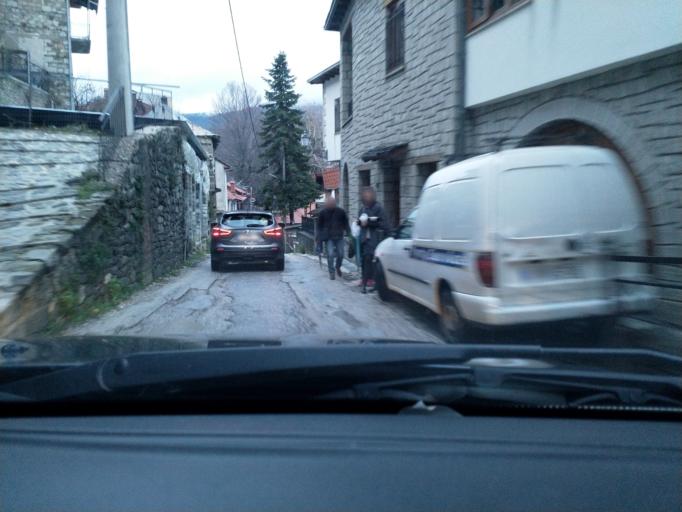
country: GR
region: Epirus
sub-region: Nomos Ioanninon
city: Metsovo
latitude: 39.7686
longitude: 21.1807
